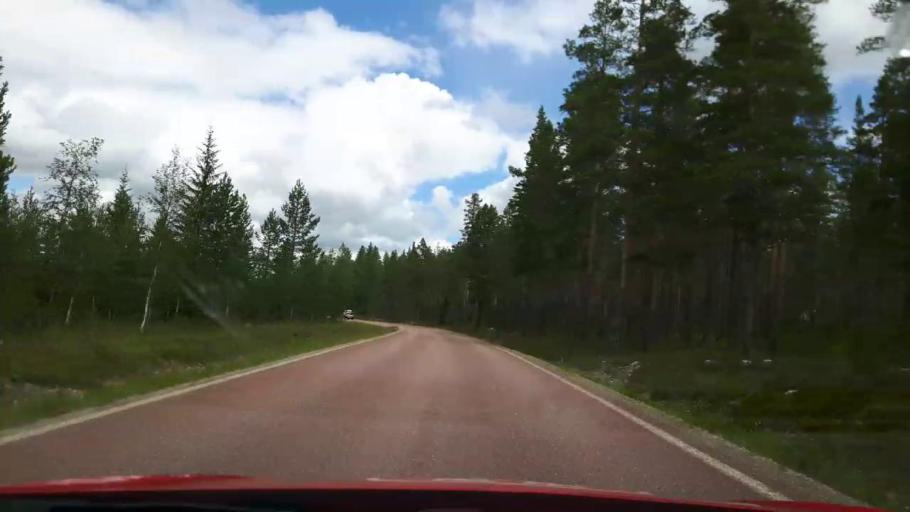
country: NO
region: Hedmark
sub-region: Trysil
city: Innbygda
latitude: 61.9110
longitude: 13.0058
